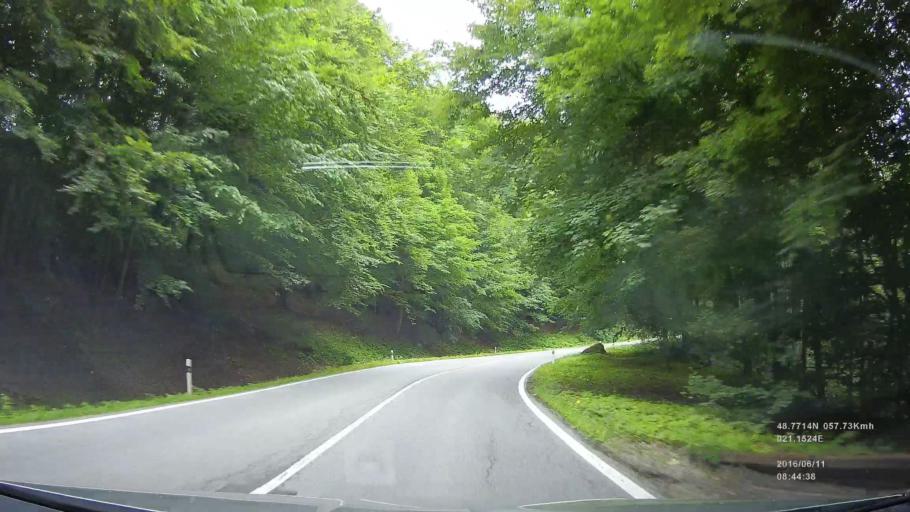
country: SK
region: Kosicky
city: Kosice
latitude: 48.7694
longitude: 21.1597
